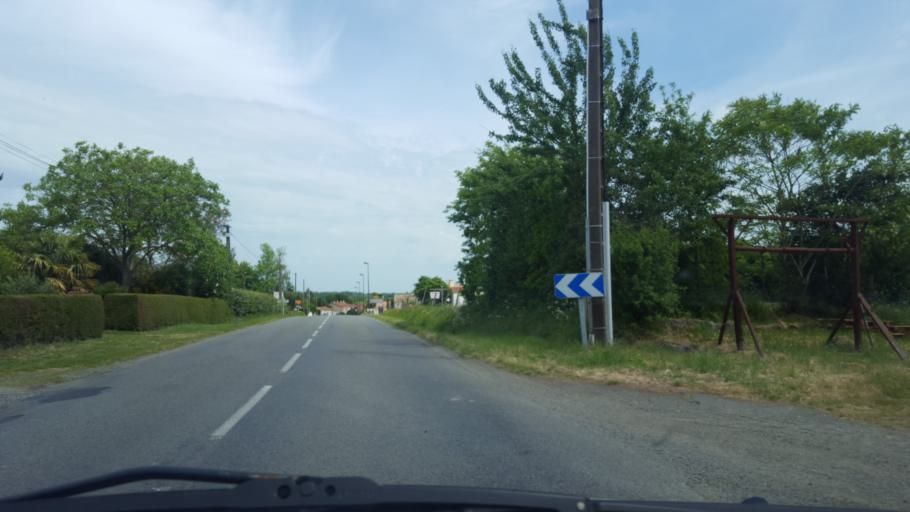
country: FR
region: Pays de la Loire
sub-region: Departement de la Loire-Atlantique
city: Montbert
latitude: 47.0544
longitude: -1.4925
